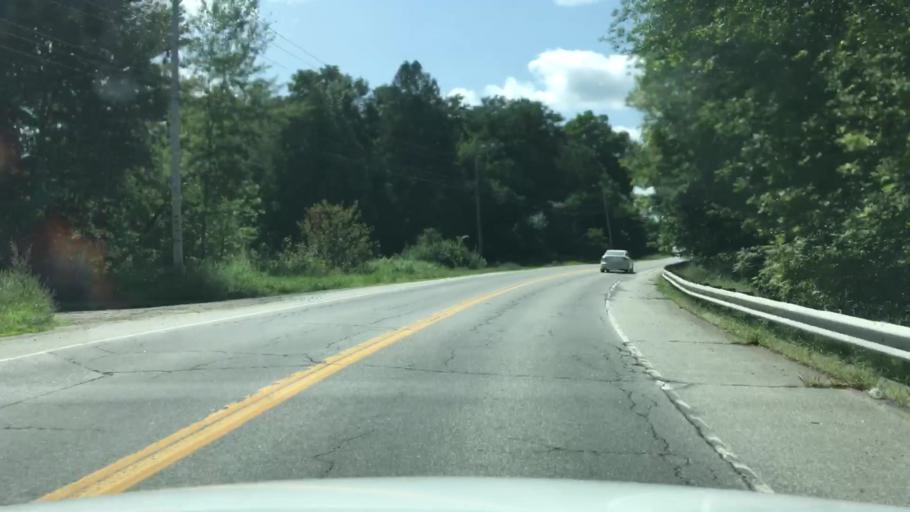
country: US
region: Maine
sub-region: Kennebec County
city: Farmingdale
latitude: 44.2431
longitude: -69.7654
